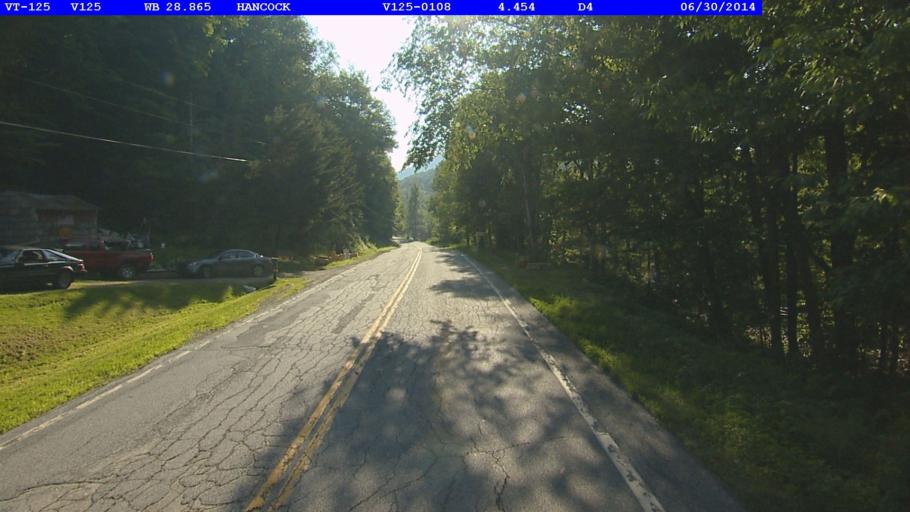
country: US
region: Vermont
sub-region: Orange County
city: Randolph
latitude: 43.9292
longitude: -72.8943
